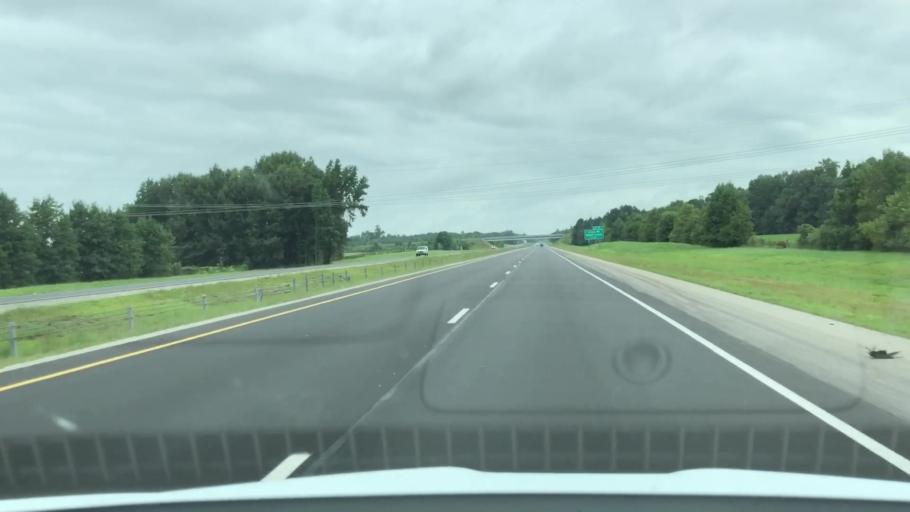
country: US
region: North Carolina
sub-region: Wilson County
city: Lucama
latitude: 35.5997
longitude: -77.9808
